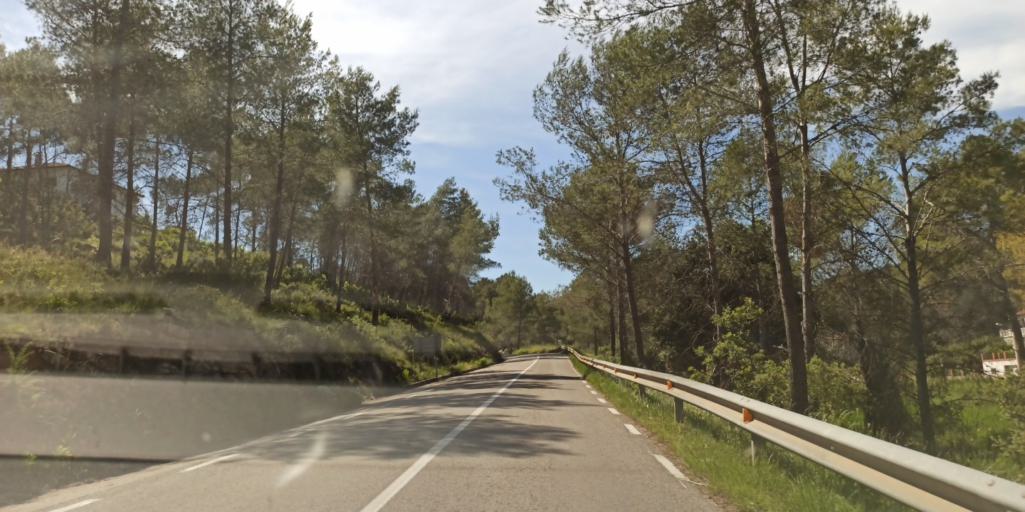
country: ES
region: Catalonia
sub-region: Provincia de Barcelona
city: Avinyonet del Penedes
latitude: 41.3137
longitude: 1.7719
